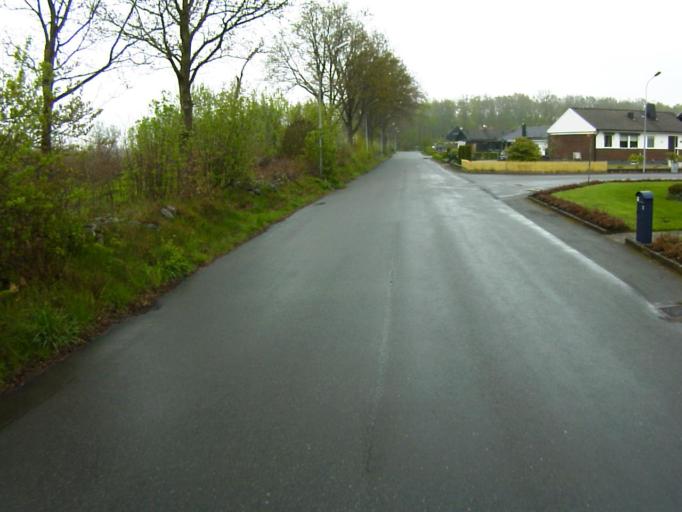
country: SE
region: Skane
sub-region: Kristianstads Kommun
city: Onnestad
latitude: 55.9371
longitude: 13.9711
